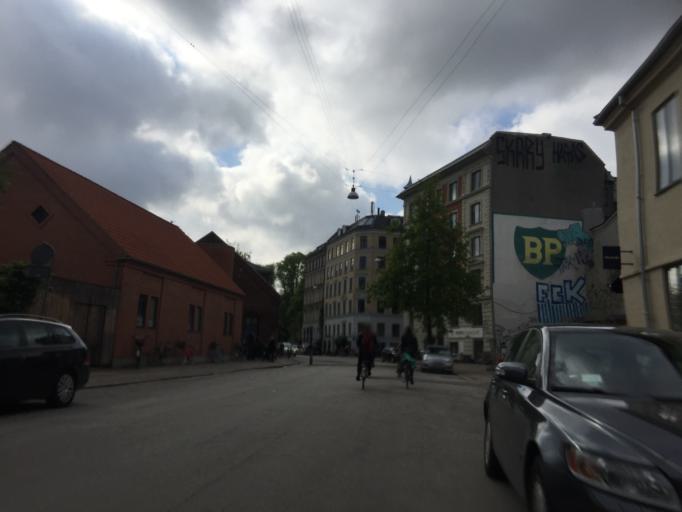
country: DK
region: Capital Region
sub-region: Kobenhavn
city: Copenhagen
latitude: 55.6926
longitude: 12.5563
